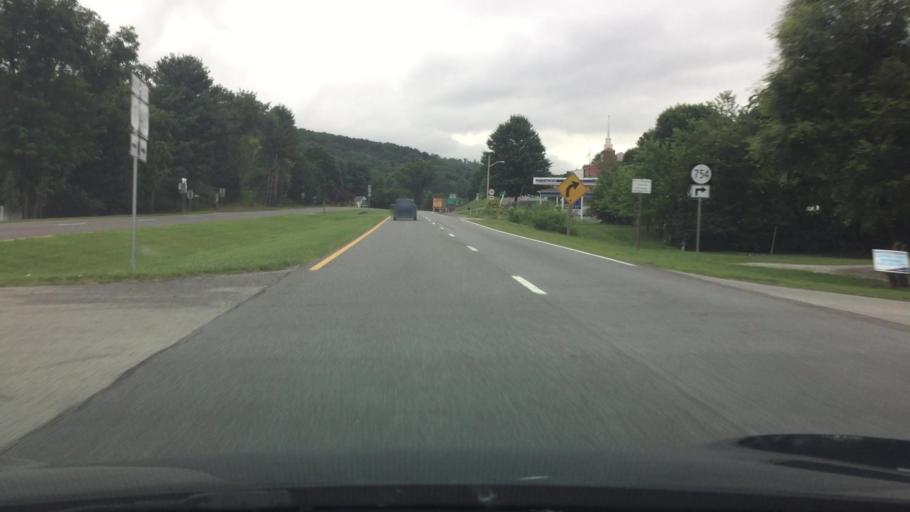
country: US
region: Virginia
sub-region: Montgomery County
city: Shawsville
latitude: 37.2162
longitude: -80.2319
